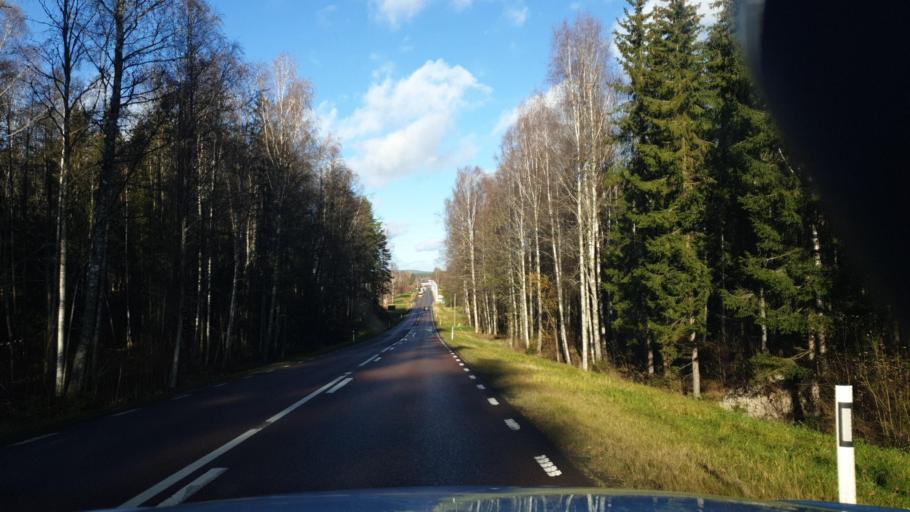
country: SE
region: Vaermland
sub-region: Arvika Kommun
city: Arvika
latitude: 59.6350
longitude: 12.6174
